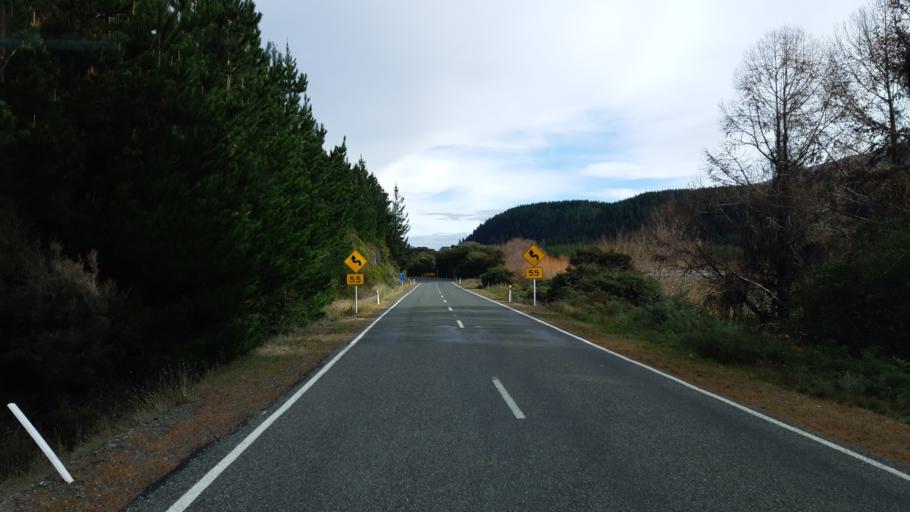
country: NZ
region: Tasman
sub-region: Tasman District
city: Wakefield
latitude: -41.7092
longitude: 173.1175
